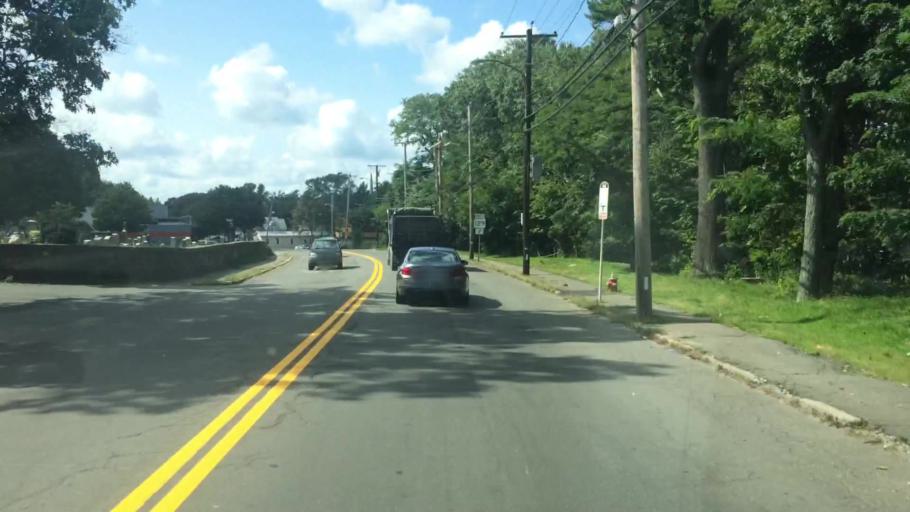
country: US
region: Massachusetts
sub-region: Essex County
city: South Peabody
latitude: 42.4904
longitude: -70.9700
